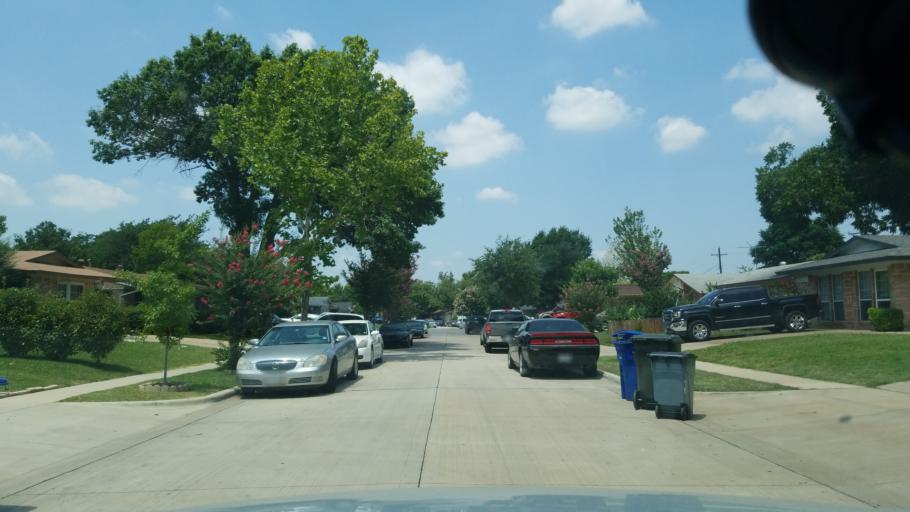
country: US
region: Texas
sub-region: Dallas County
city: Carrollton
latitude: 32.9530
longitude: -96.8737
